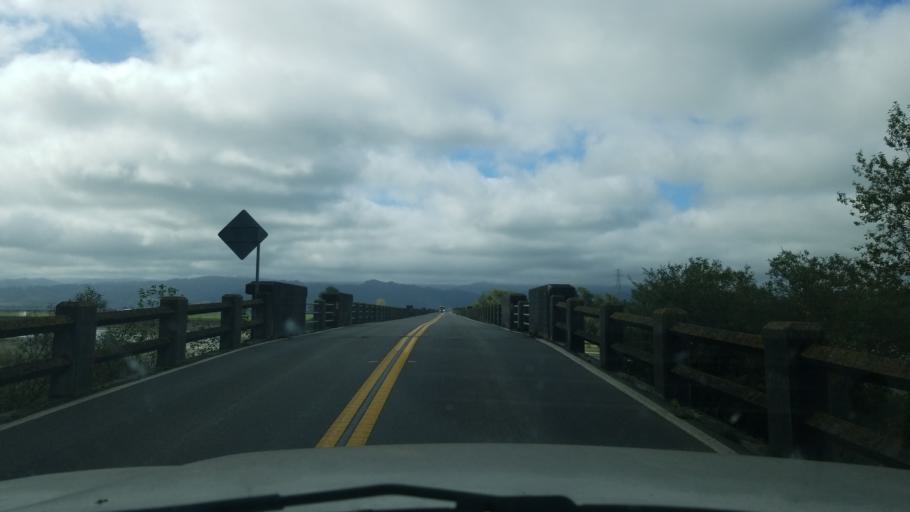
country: US
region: California
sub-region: Humboldt County
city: Fortuna
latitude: 40.6149
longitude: -124.2026
